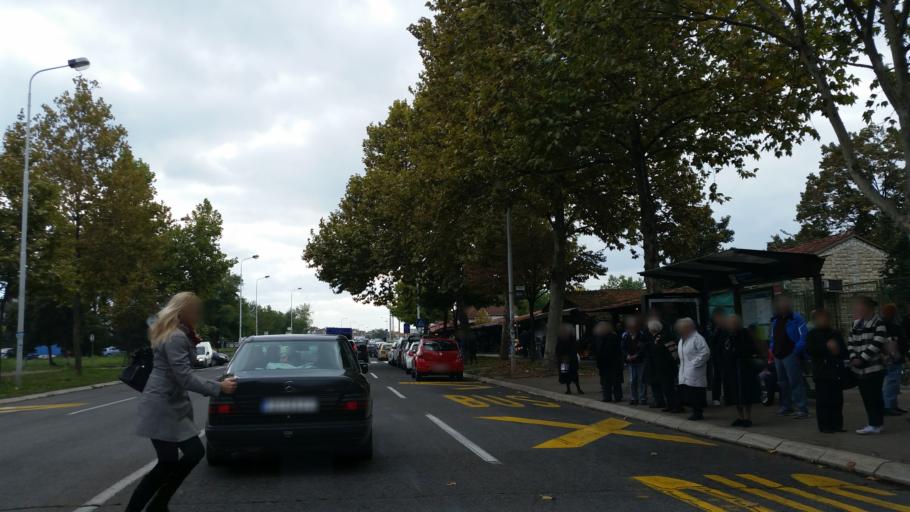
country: RS
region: Central Serbia
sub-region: Belgrade
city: Zemun
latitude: 44.8176
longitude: 20.3713
